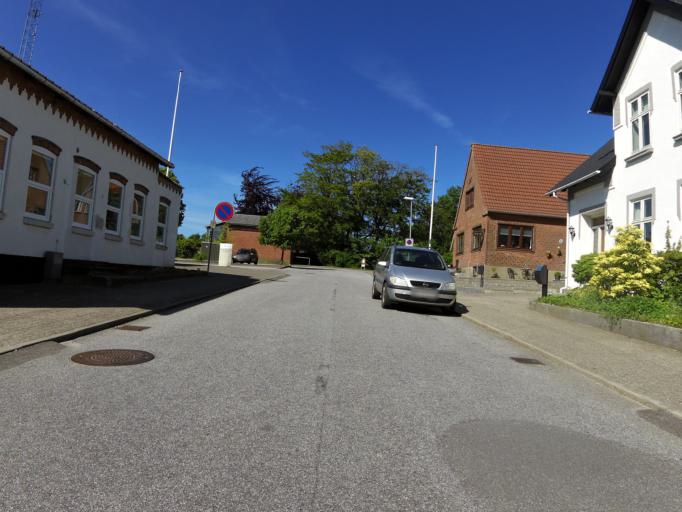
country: DK
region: South Denmark
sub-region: Haderslev Kommune
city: Gram
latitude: 55.2891
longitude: 9.0491
